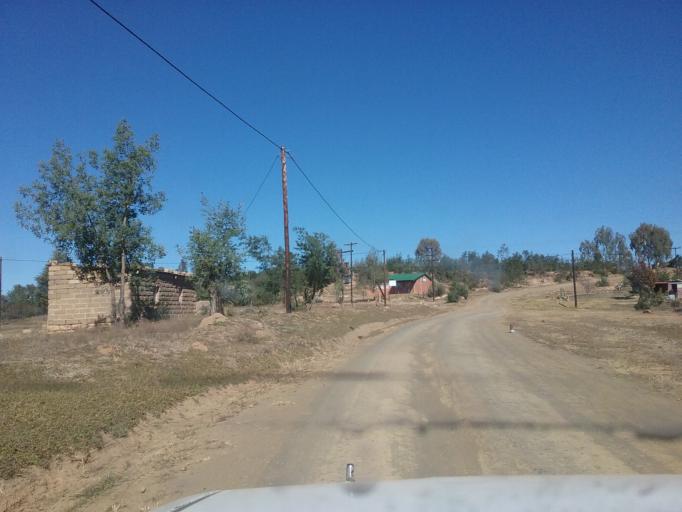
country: LS
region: Maseru
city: Maseru
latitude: -29.4487
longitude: 27.5795
